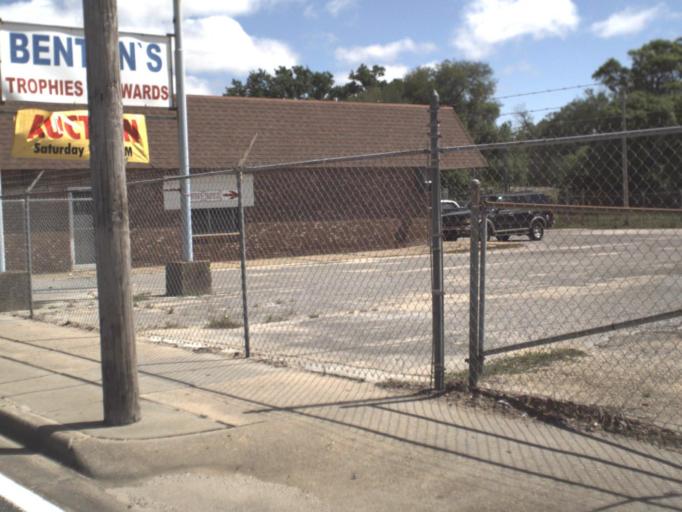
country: US
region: Florida
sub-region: Escambia County
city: Goulding
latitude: 30.4306
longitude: -87.2406
